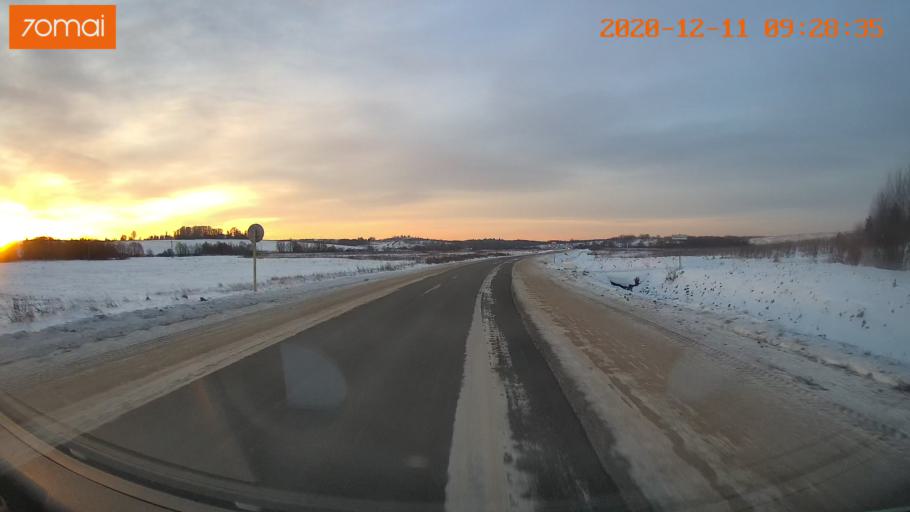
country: RU
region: Vologda
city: Vologda
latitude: 59.1515
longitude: 40.0076
